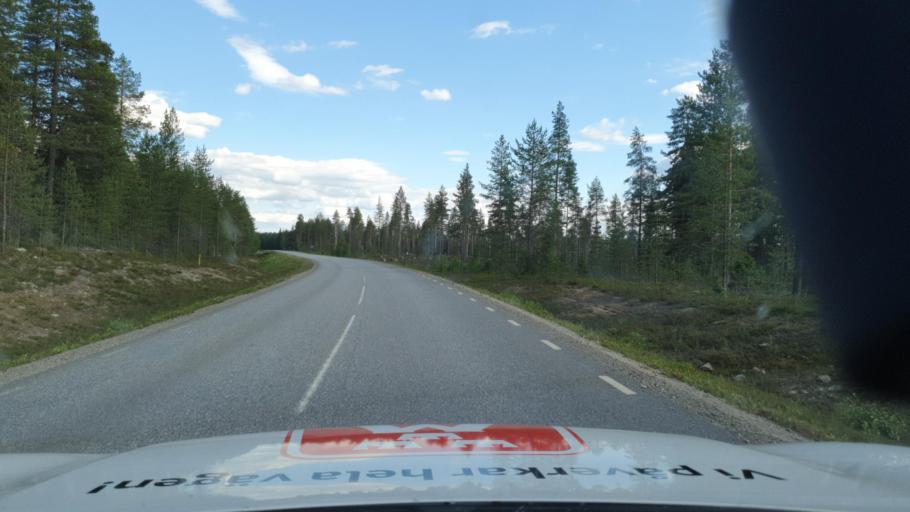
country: SE
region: Vaesterbotten
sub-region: Skelleftea Kommun
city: Langsele
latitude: 64.8098
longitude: 19.9930
